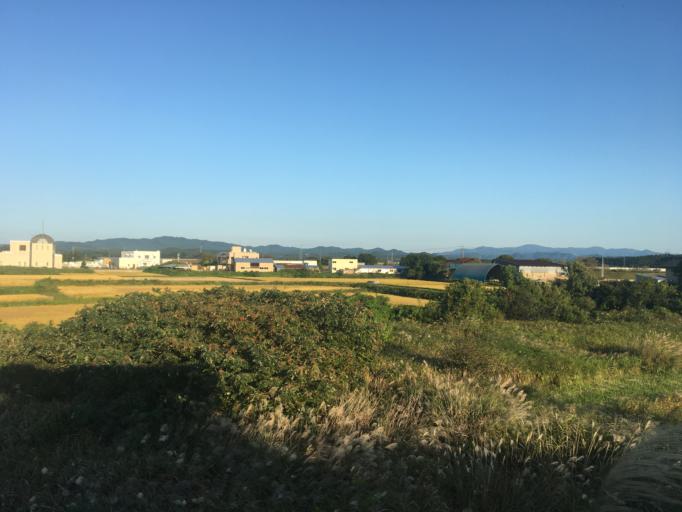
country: JP
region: Akita
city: Takanosu
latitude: 40.2163
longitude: 140.3548
